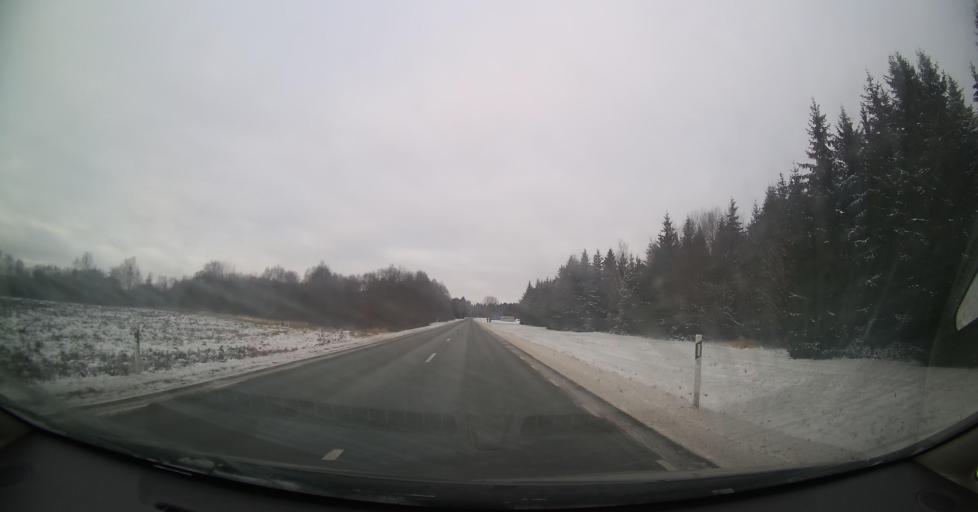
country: EE
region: Harju
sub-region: Anija vald
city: Kehra
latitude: 59.3072
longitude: 25.3530
